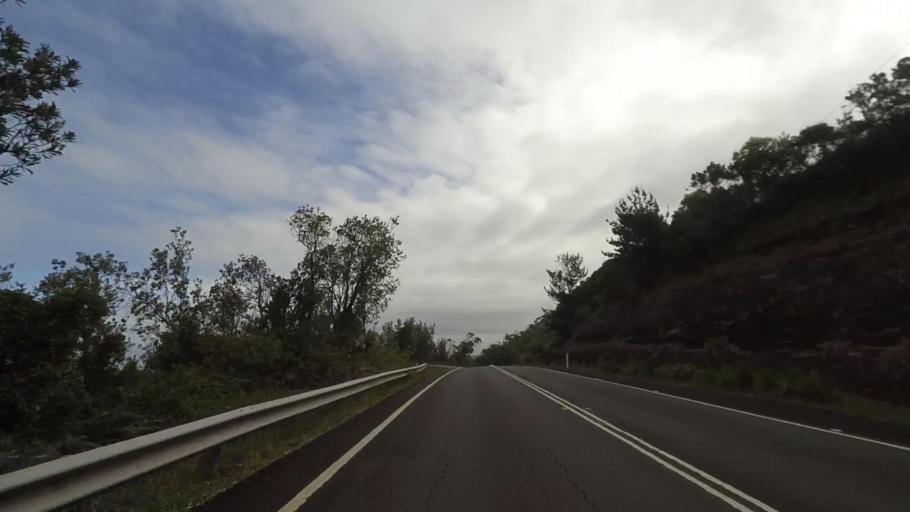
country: AU
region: New South Wales
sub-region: Wollongong
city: Helensburgh
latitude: -34.2163
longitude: 151.0044
